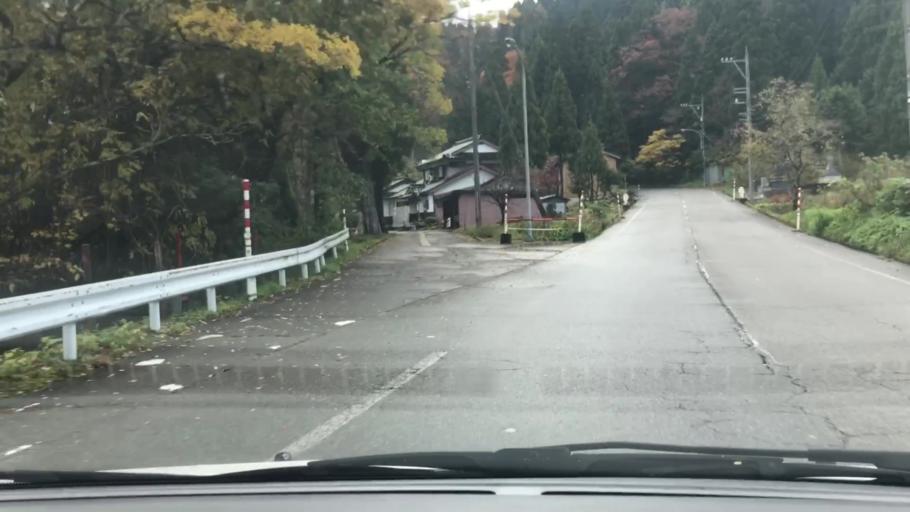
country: JP
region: Toyama
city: Kamiichi
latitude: 36.5848
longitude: 137.3238
